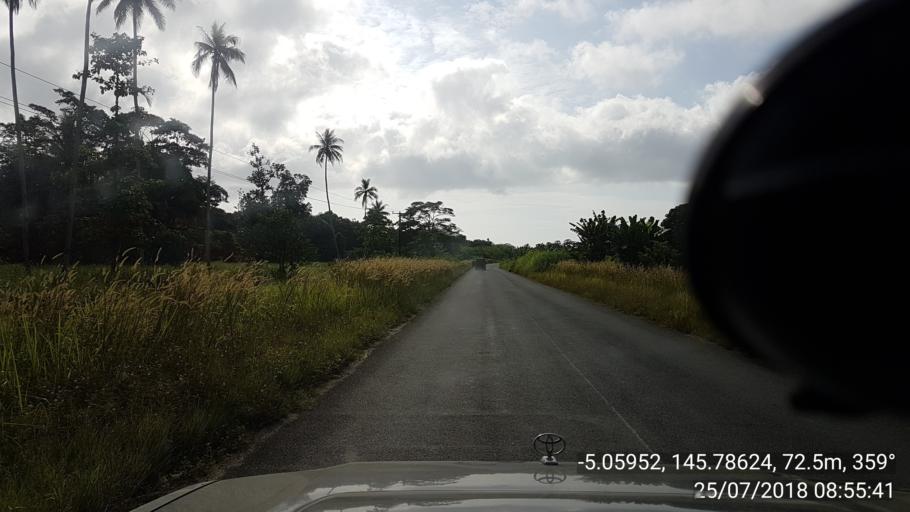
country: PG
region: Madang
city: Madang
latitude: -5.0595
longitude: 145.7861
